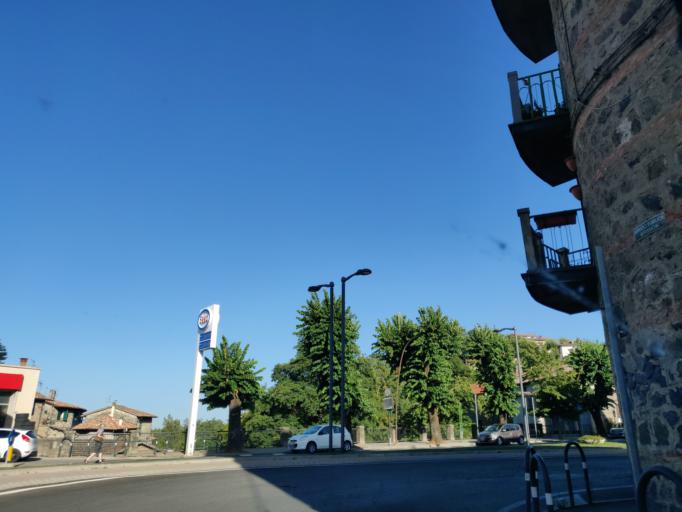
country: IT
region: Tuscany
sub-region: Provincia di Siena
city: Abbadia San Salvatore
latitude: 42.8779
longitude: 11.6786
